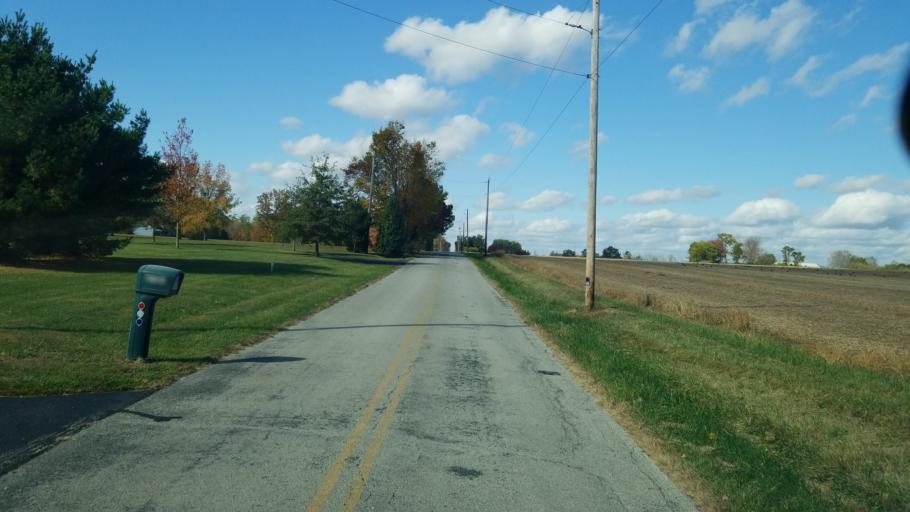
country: US
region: Ohio
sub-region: Warren County
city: Morrow
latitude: 39.4010
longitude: -84.1562
